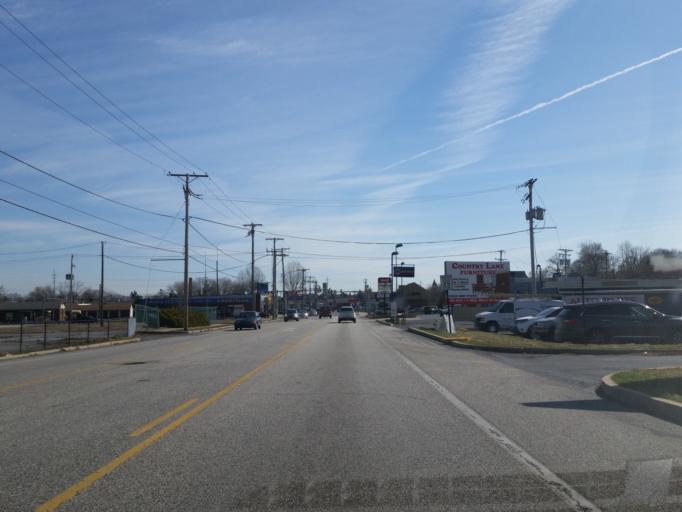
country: US
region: Pennsylvania
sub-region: Lebanon County
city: Pleasant Hill
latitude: 40.3383
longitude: -76.4415
